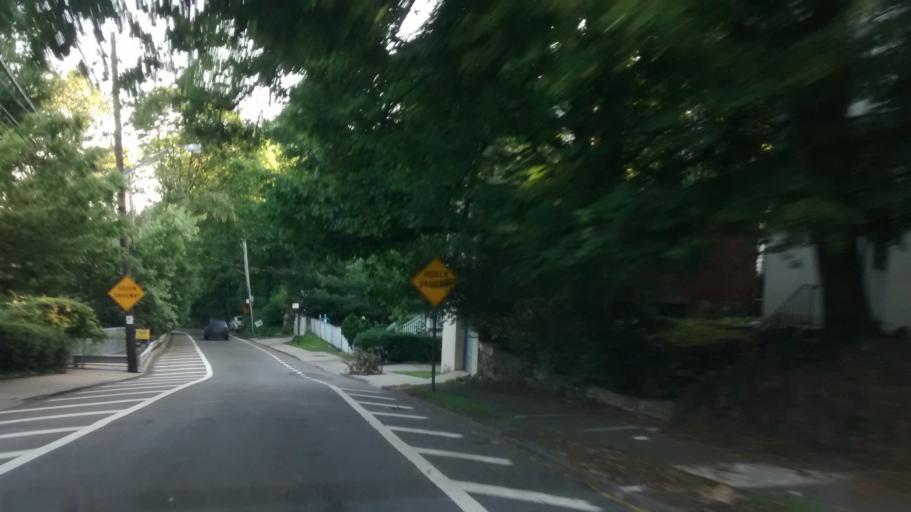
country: US
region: New Jersey
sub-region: Hudson County
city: Bayonne
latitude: 40.6278
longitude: -74.0836
